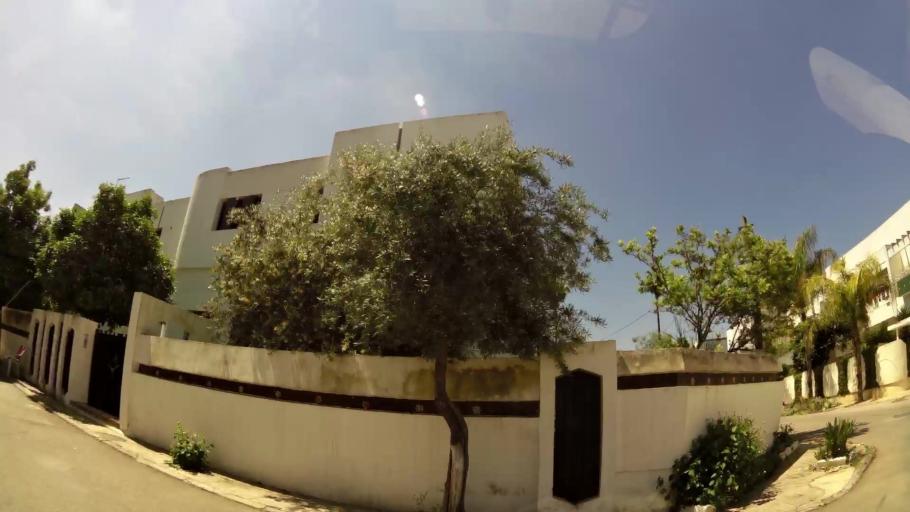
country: MA
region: Fes-Boulemane
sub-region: Fes
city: Fes
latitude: 34.0304
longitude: -5.0131
